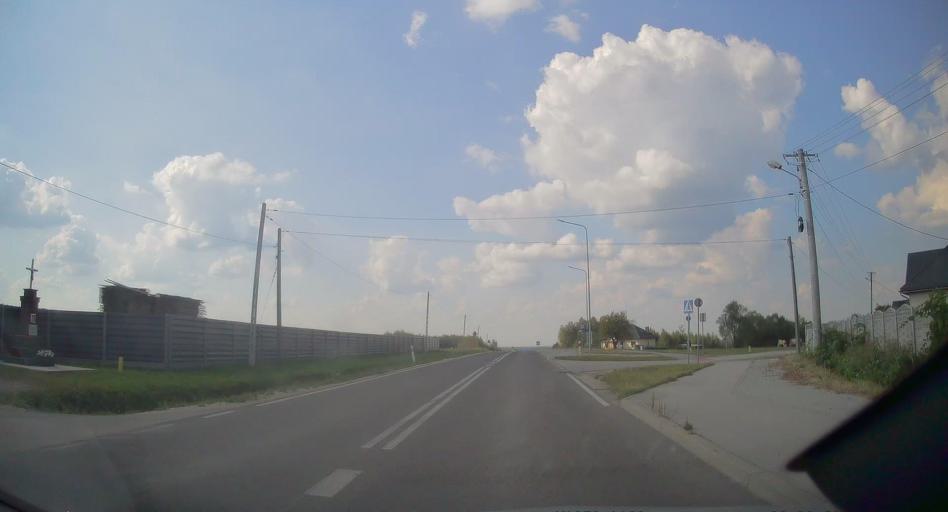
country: PL
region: Swietokrzyskie
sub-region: Powiat konecki
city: Radoszyce
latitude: 51.0343
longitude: 20.2865
